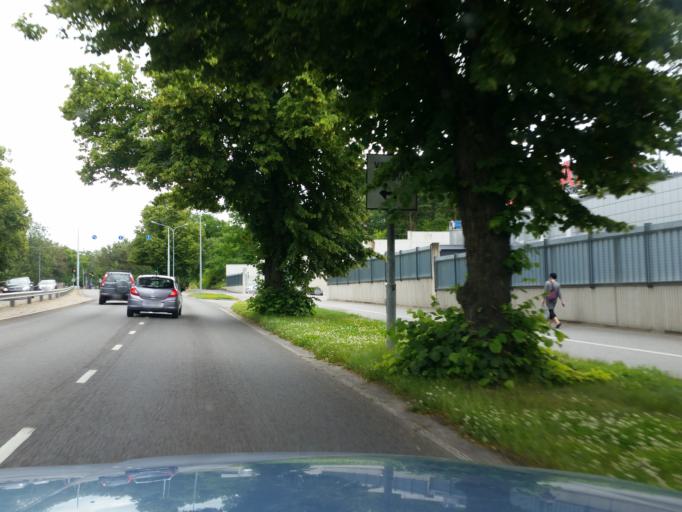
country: FI
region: Varsinais-Suomi
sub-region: Turku
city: Turku
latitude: 60.4425
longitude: 22.2877
